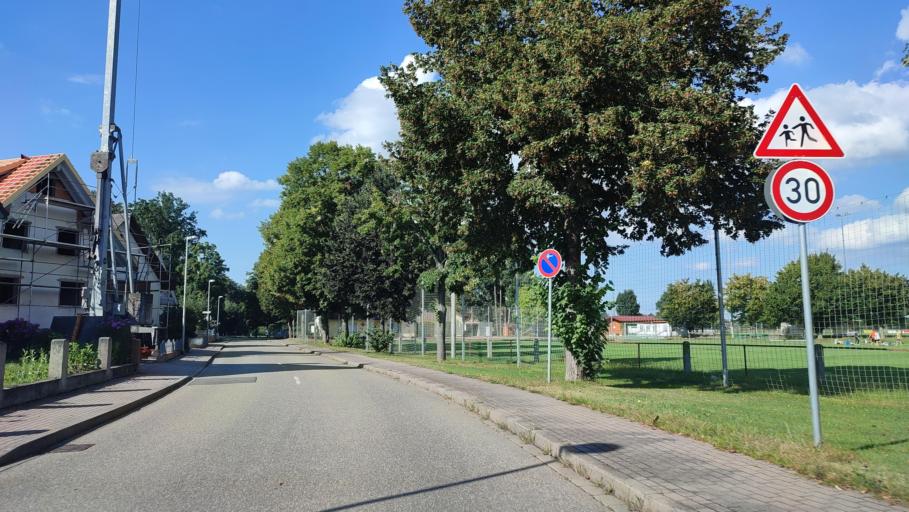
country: DE
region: Baden-Wuerttemberg
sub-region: Freiburg Region
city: Renchen
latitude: 48.5511
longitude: 8.0201
